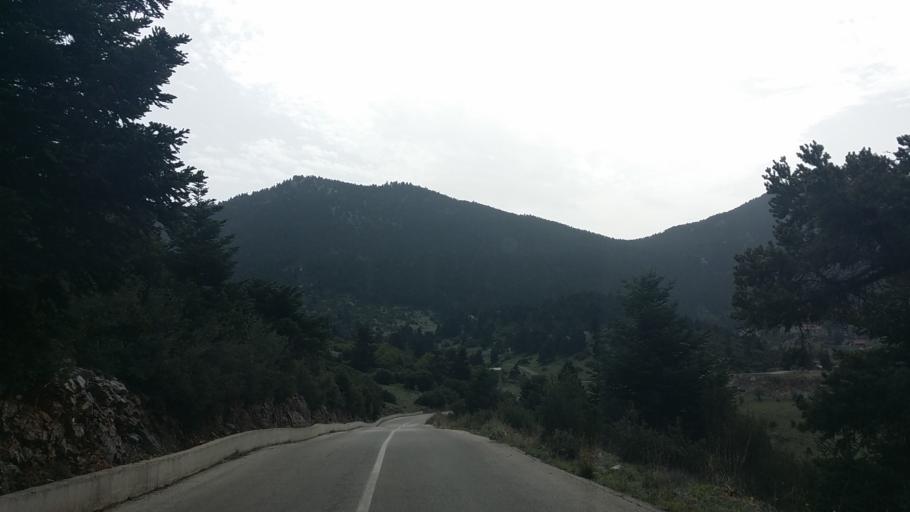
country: GR
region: Central Greece
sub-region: Nomos Voiotias
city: Livadeia
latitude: 38.3785
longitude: 22.8440
